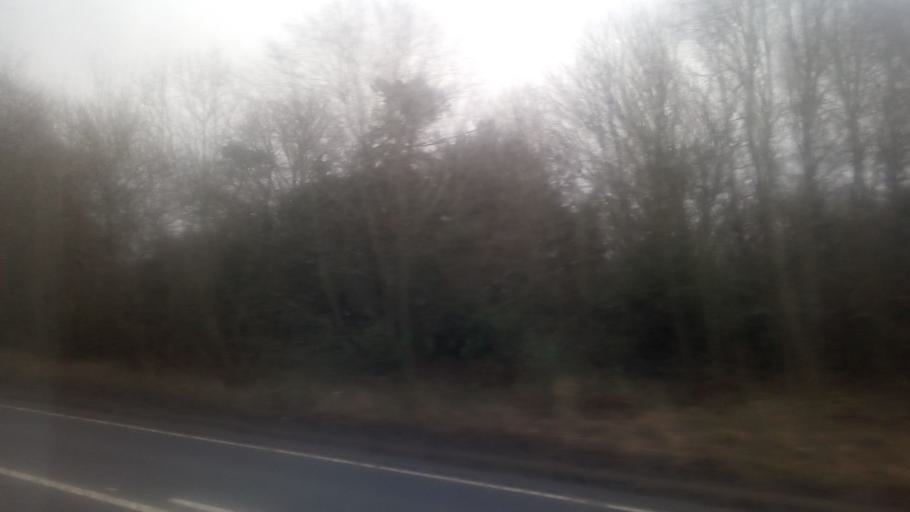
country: GB
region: Scotland
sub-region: The Scottish Borders
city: Newtown St Boswells
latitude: 55.6092
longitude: -2.6755
